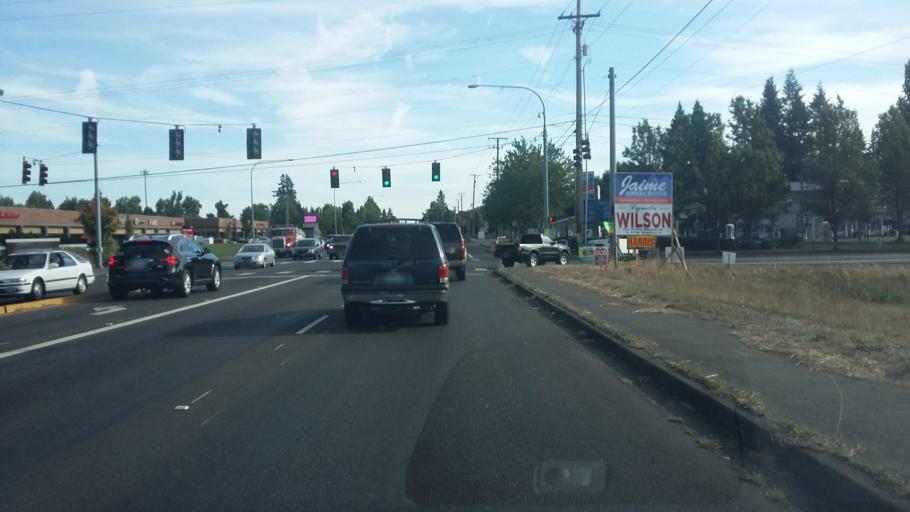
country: US
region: Washington
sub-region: Clark County
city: Five Corners
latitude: 45.6939
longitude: -122.5529
